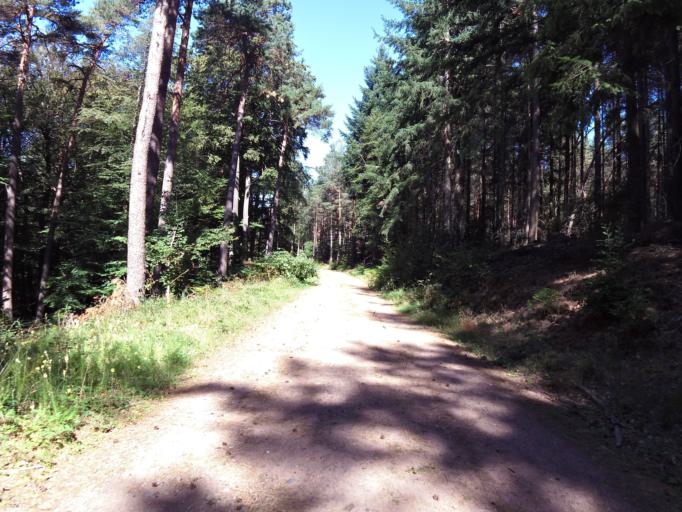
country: DE
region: Rheinland-Pfalz
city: Esthal
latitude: 49.3976
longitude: 7.9684
